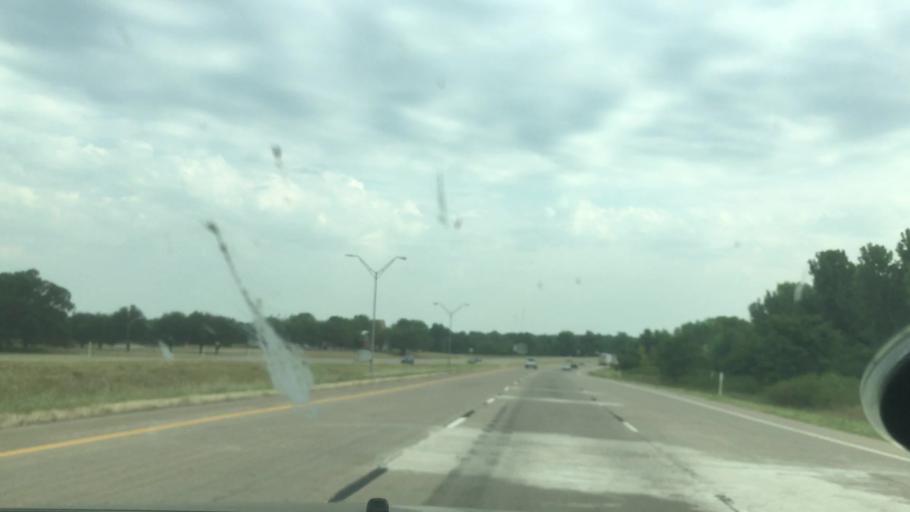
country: US
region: Oklahoma
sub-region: Bryan County
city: Colbert
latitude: 33.8152
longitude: -96.5349
